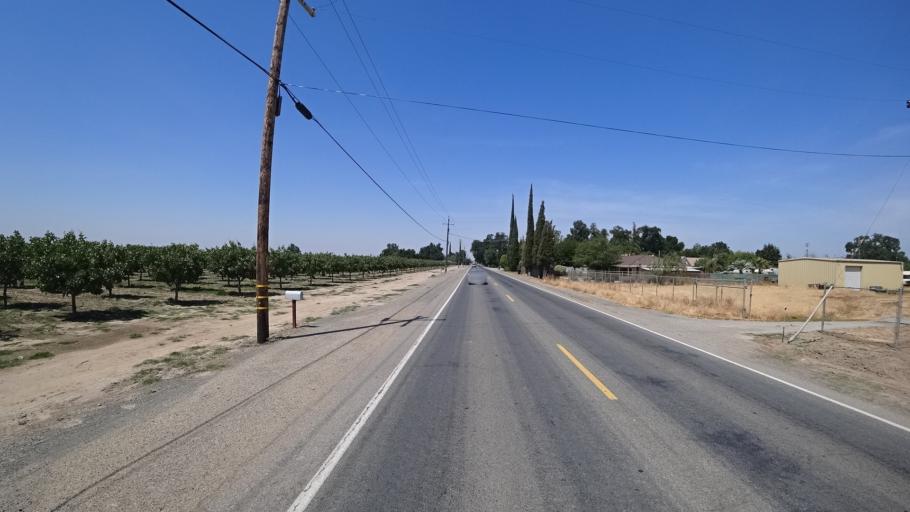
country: US
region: California
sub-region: Kings County
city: Lucerne
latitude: 36.4012
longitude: -119.6782
